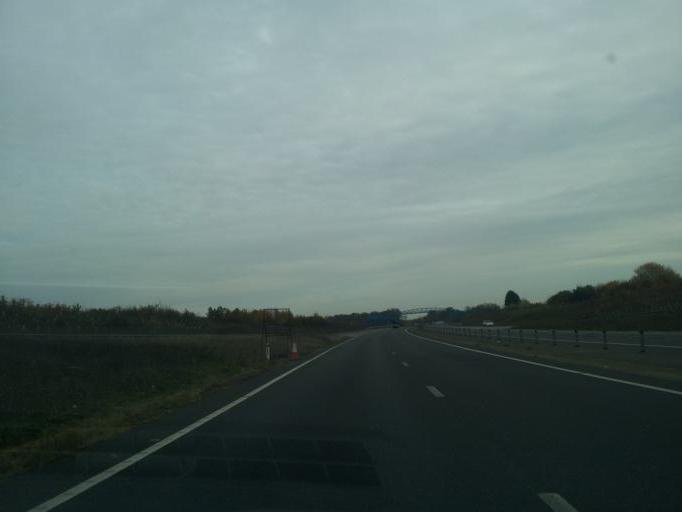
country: GB
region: England
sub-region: Cambridgeshire
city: Comberton
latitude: 52.2200
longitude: 0.0038
